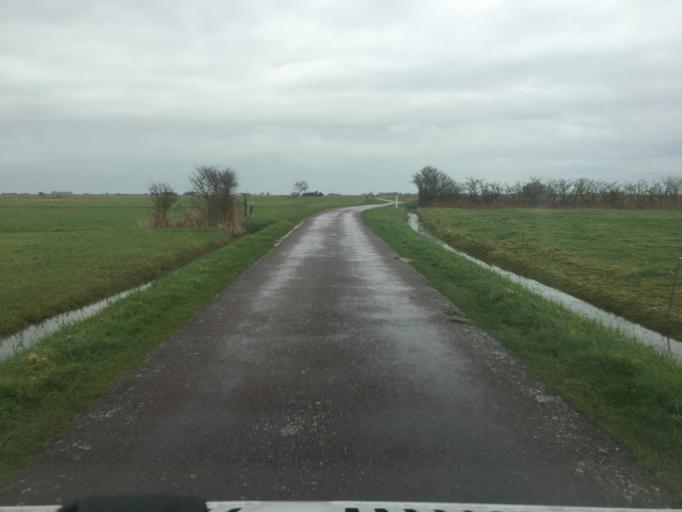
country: FR
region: Lower Normandy
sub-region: Departement de la Manche
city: Sainte-Mere-Eglise
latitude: 49.4448
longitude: -1.2409
